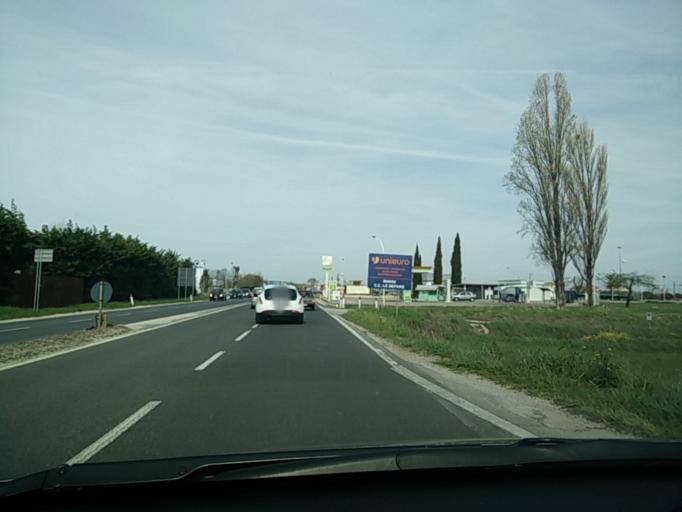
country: IT
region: Emilia-Romagna
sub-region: Provincia di Rimini
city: Santa Giustina
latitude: 44.0690
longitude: 12.5206
